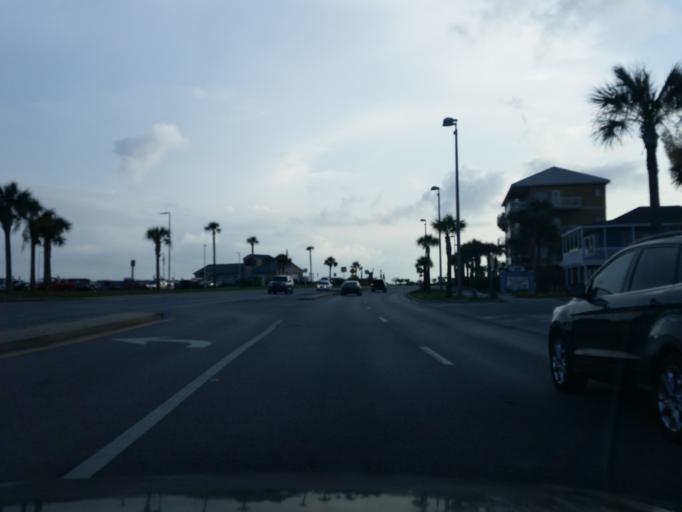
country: US
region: Florida
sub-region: Santa Rosa County
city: Gulf Breeze
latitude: 30.3326
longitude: -87.1422
